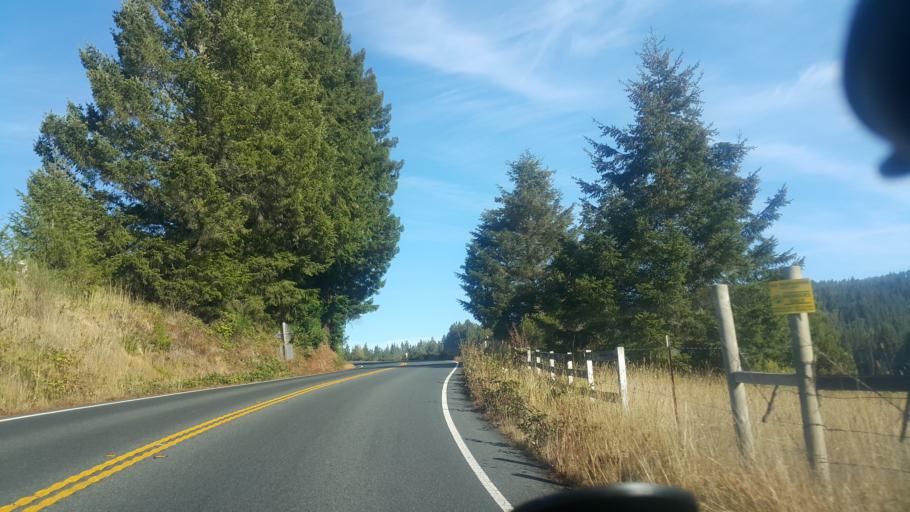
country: US
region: California
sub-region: Mendocino County
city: Fort Bragg
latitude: 39.3544
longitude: -123.6146
